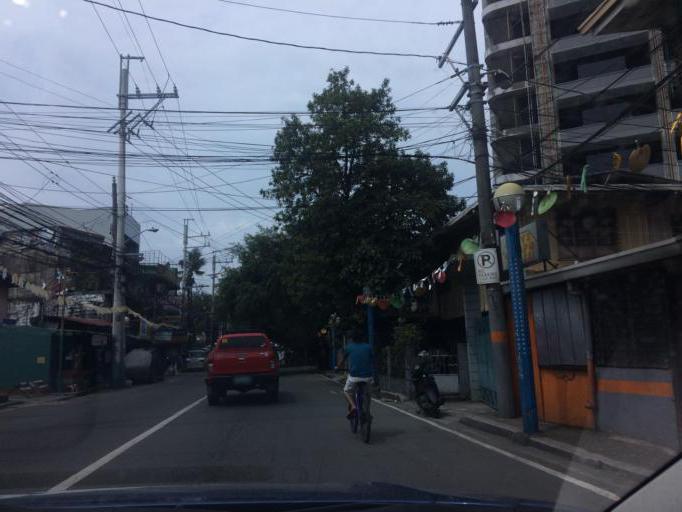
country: PH
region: Metro Manila
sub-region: Makati City
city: Makati City
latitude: 14.5485
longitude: 121.0039
